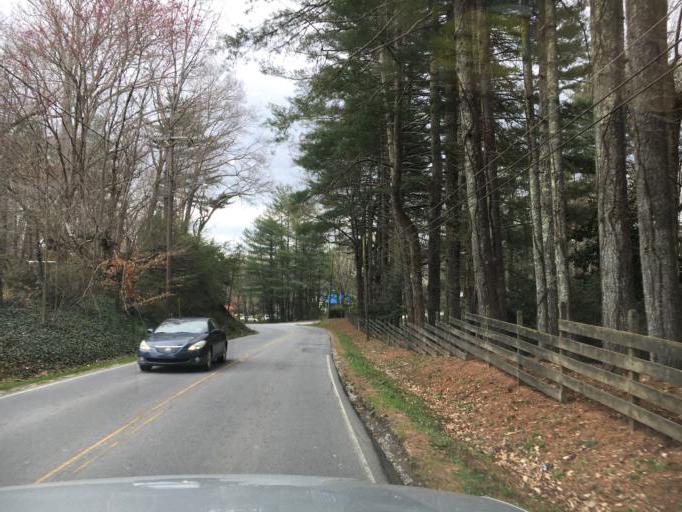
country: US
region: North Carolina
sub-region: Transylvania County
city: Brevard
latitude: 35.2328
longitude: -82.7226
